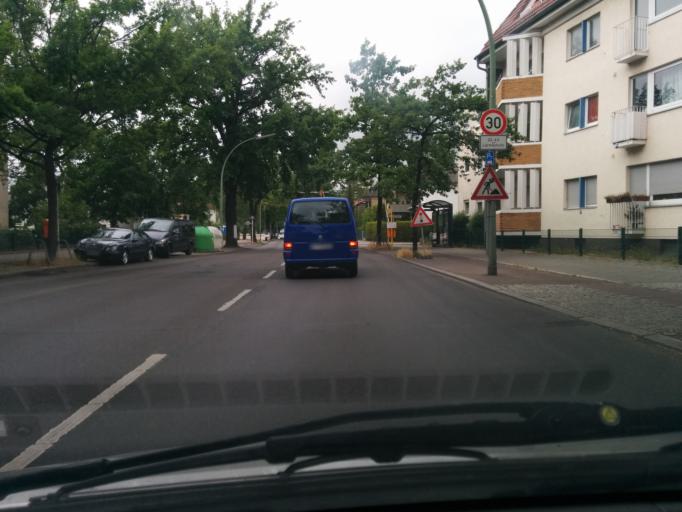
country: DE
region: Berlin
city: Falkenhagener Feld
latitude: 52.5400
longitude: 13.1753
